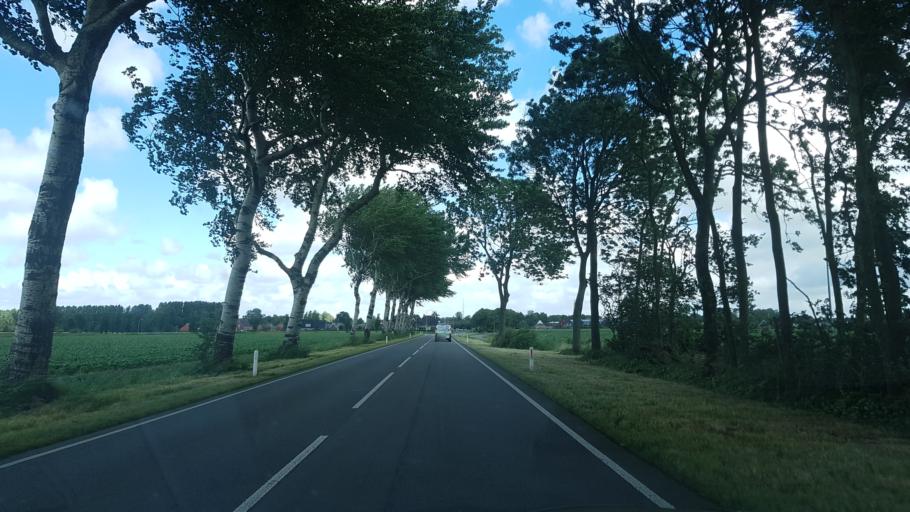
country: NL
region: Groningen
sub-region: Gemeente Winsum
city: Winsum
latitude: 53.3892
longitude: 6.5435
